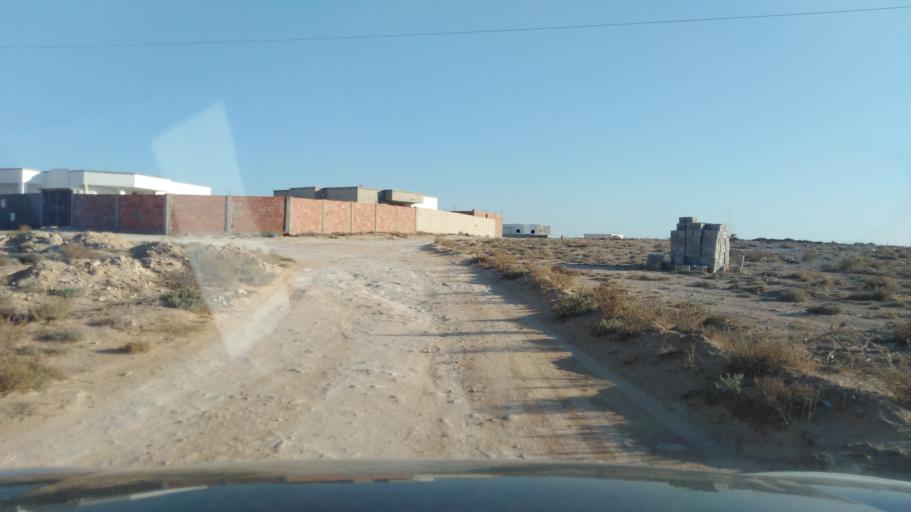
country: TN
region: Qabis
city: Gabes
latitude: 33.9503
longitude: 10.0117
